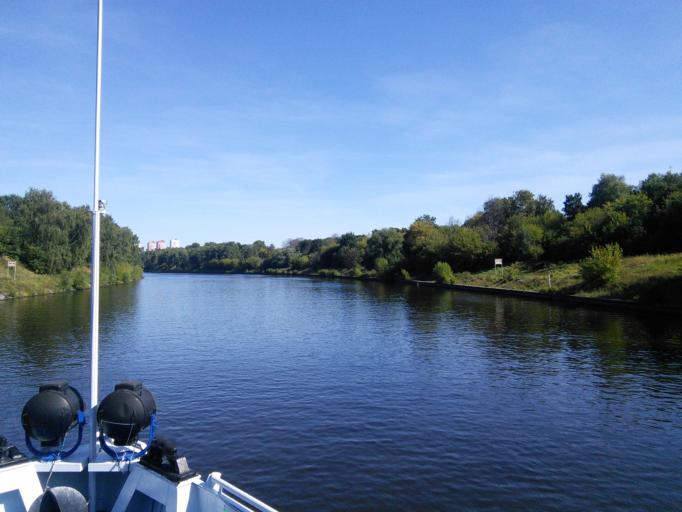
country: RU
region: Moskovskaya
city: Levoberezhnaya
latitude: 55.9154
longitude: 37.4857
